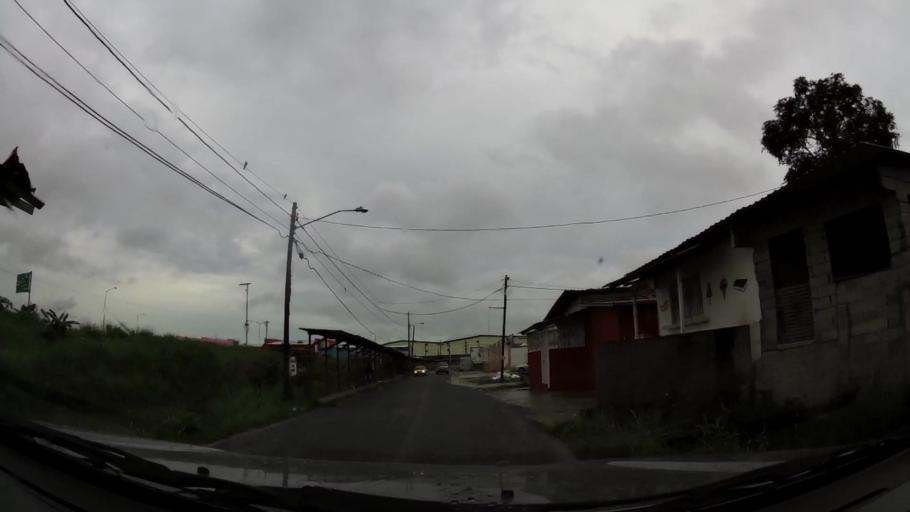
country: PA
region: Colon
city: Arco Iris
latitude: 9.3368
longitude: -79.8799
